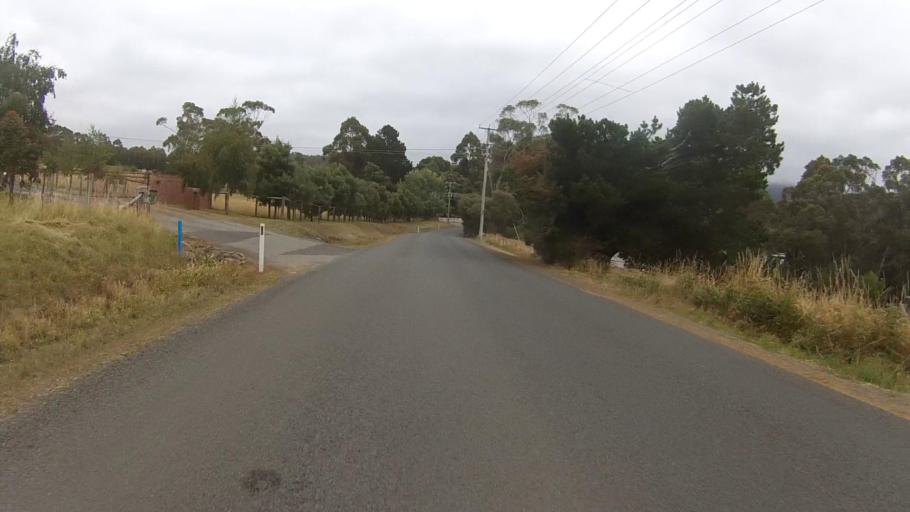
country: AU
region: Tasmania
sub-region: Kingborough
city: Kingston
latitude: -42.9655
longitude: 147.2851
